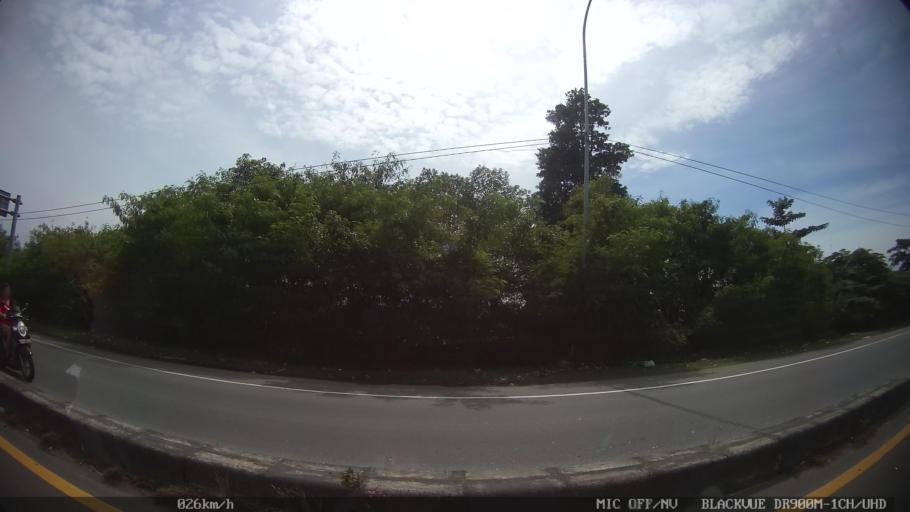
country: ID
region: North Sumatra
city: Sunggal
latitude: 3.6166
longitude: 98.6286
